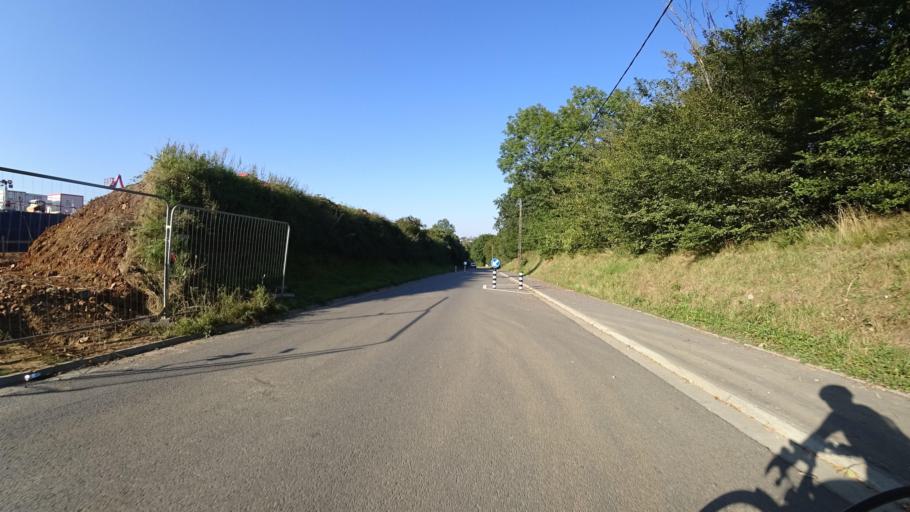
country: BE
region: Wallonia
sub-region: Province de Namur
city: Namur
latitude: 50.4645
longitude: 4.8315
